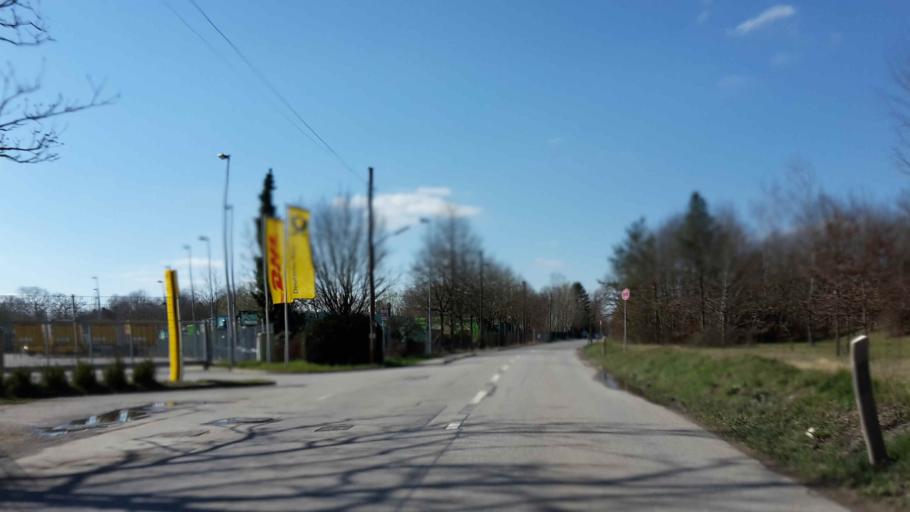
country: DE
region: Bavaria
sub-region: Upper Bavaria
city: Karlsfeld
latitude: 48.1932
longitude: 11.4960
